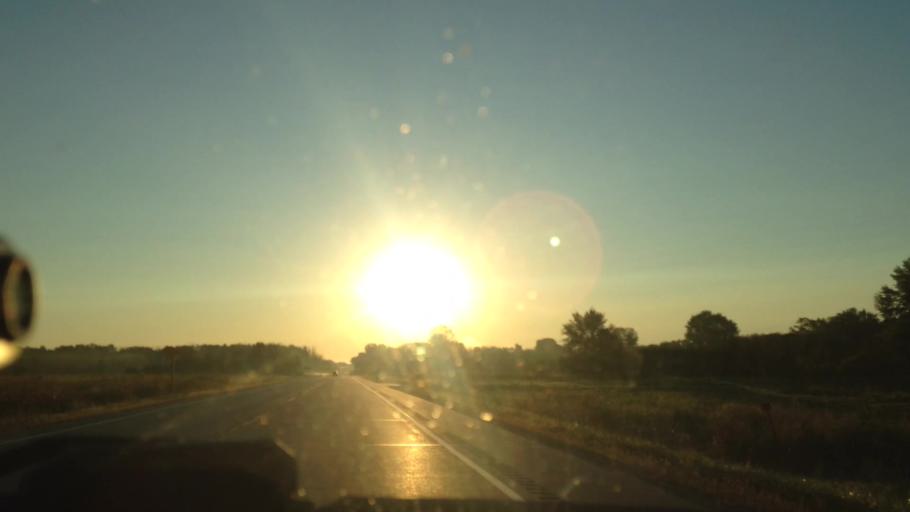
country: US
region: Wisconsin
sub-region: Washington County
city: West Bend
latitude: 43.4263
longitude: -88.1202
